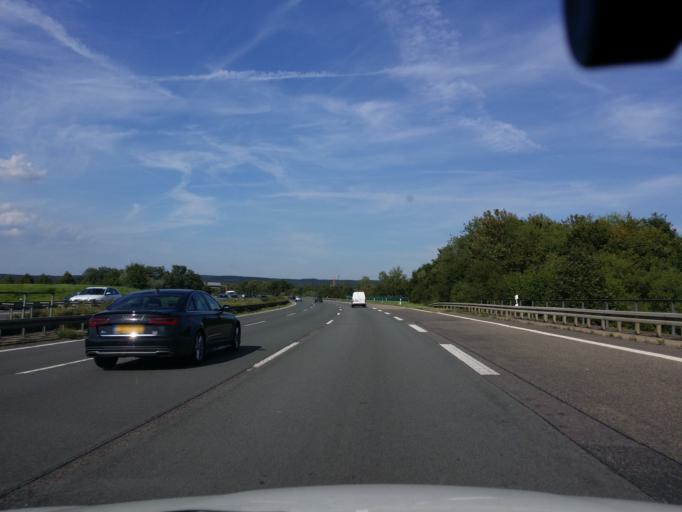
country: DE
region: North Rhine-Westphalia
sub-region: Regierungsbezirk Koln
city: Stossdorf
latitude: 50.7760
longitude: 7.2409
